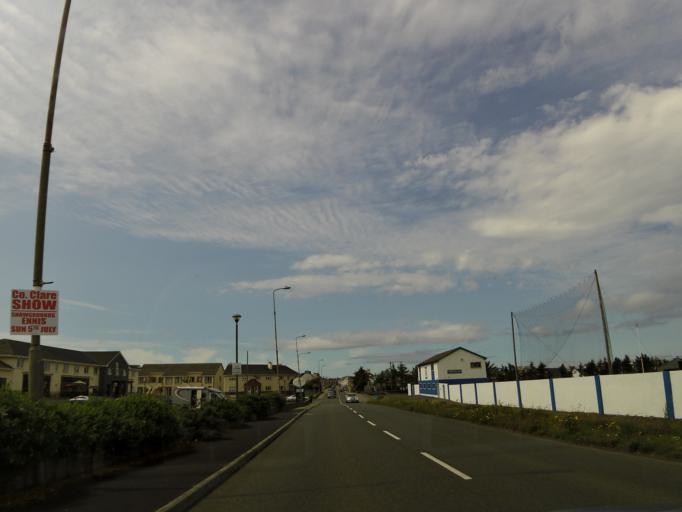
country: IE
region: Munster
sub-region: An Clar
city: Kilrush
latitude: 52.6779
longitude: -9.6396
